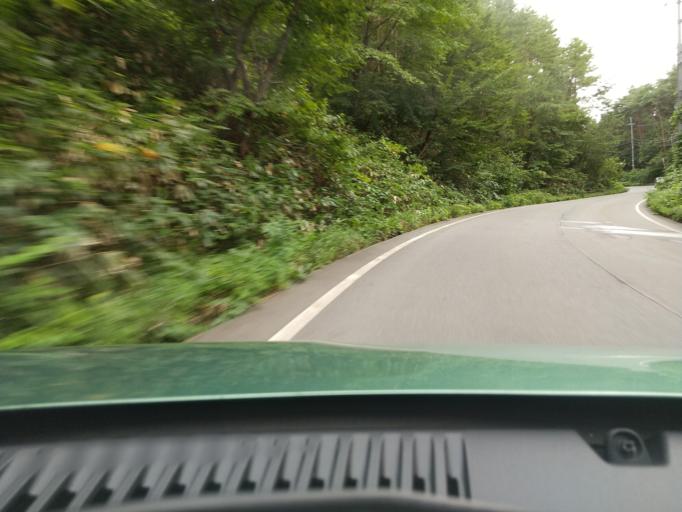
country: JP
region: Akita
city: Akita
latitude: 39.7729
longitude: 140.1340
